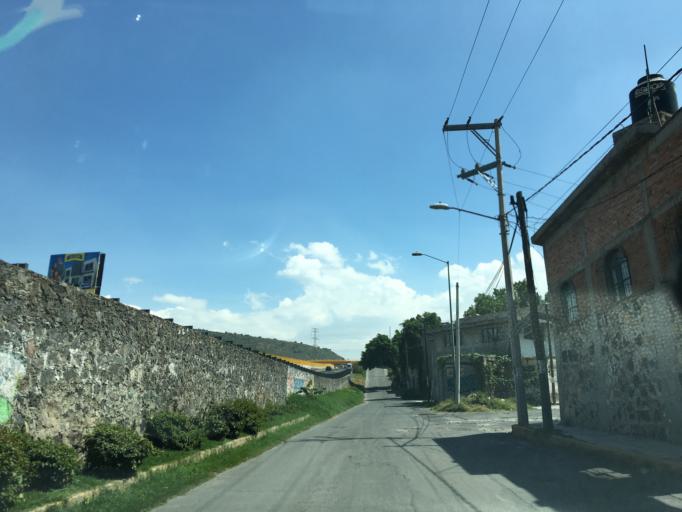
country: MX
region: Mexico
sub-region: La Paz
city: Emiliano Zapata
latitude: 19.3499
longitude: -98.9861
